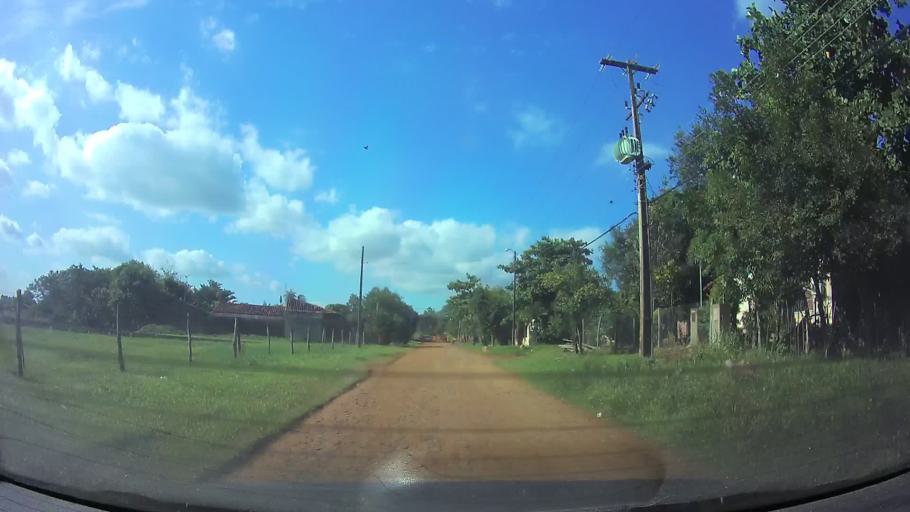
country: PY
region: Central
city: Limpio
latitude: -25.2474
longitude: -57.4698
